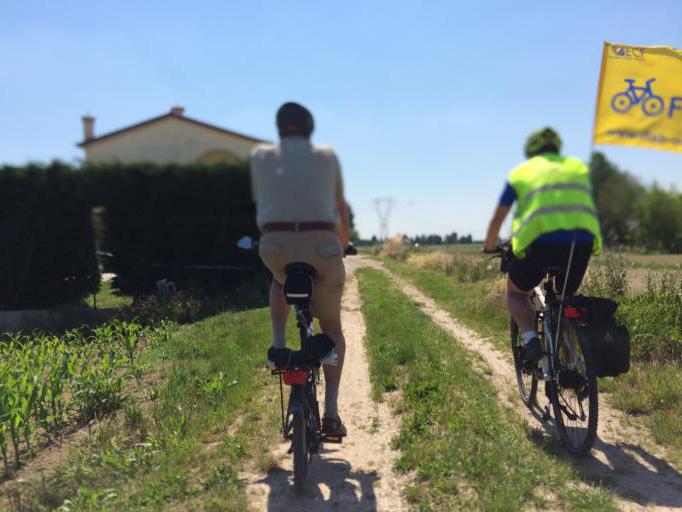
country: IT
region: Veneto
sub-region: Provincia di Vicenza
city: Sossano
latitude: 45.3443
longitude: 11.4861
